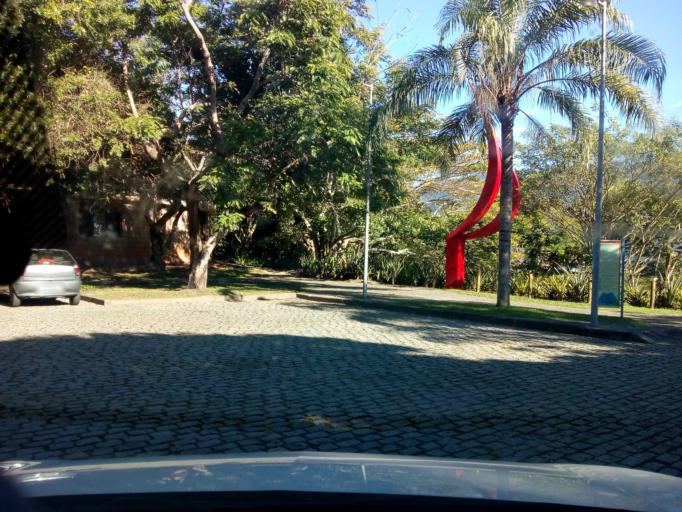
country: BR
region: Rio de Janeiro
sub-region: Rio De Janeiro
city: Rio de Janeiro
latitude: -22.9887
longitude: -43.2310
